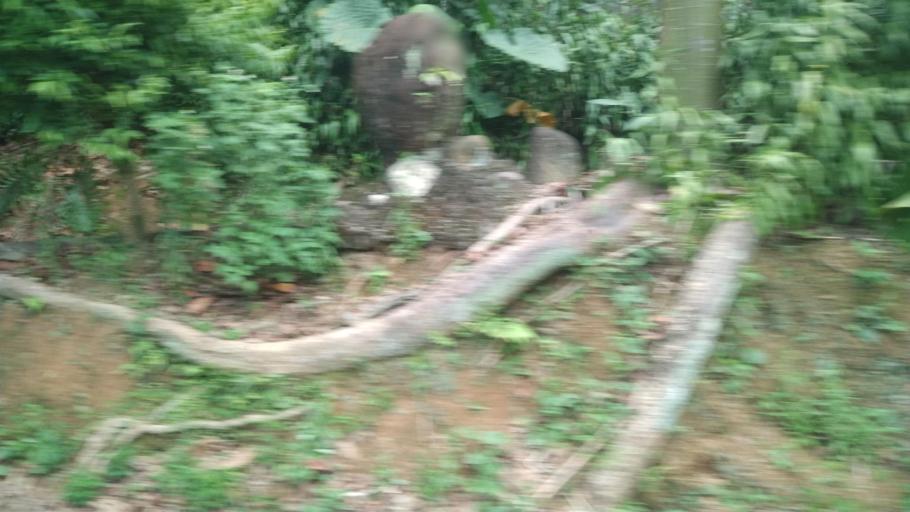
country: TW
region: Taipei
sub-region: Taipei
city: Banqiao
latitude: 24.9182
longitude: 121.4170
